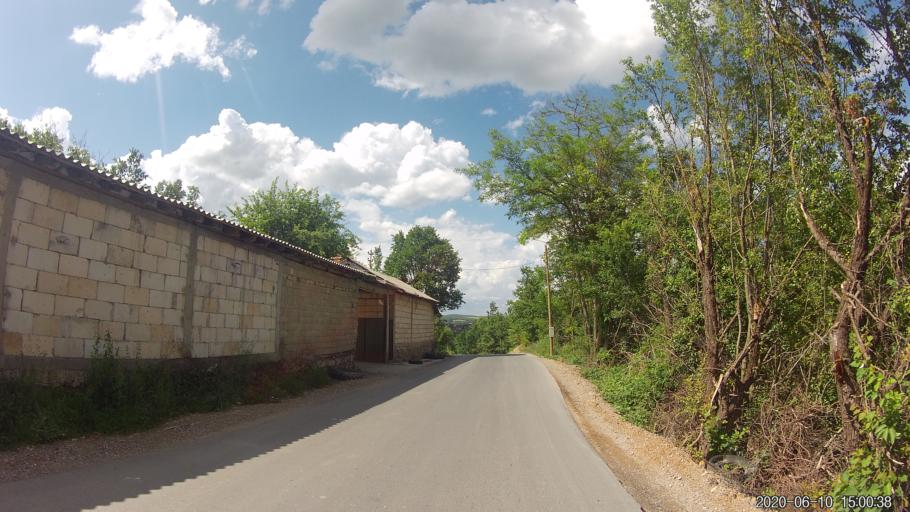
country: XK
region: Ferizaj
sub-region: Komuna e Shtimes
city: Shtime
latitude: 42.4131
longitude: 21.0326
